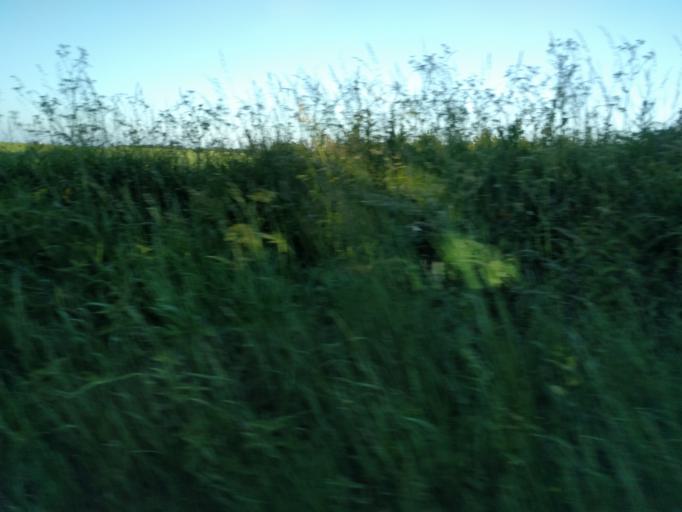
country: DK
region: South Denmark
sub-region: Kerteminde Kommune
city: Kerteminde
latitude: 55.5688
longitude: 10.6469
